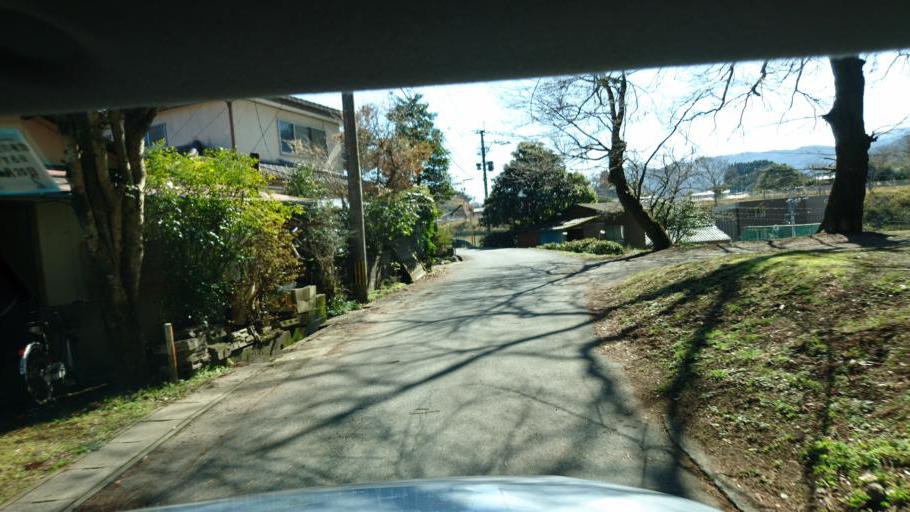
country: JP
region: Oita
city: Takedamachi
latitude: 32.7179
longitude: 131.3062
